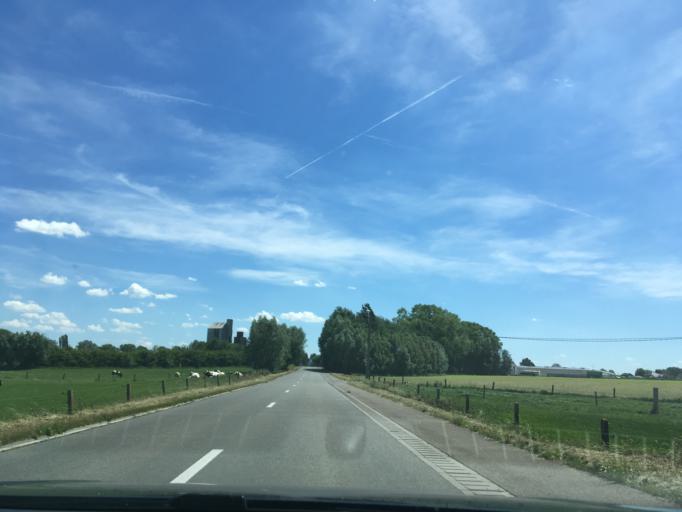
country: BE
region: Flanders
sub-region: Provincie West-Vlaanderen
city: Hooglede
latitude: 51.0147
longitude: 3.0764
